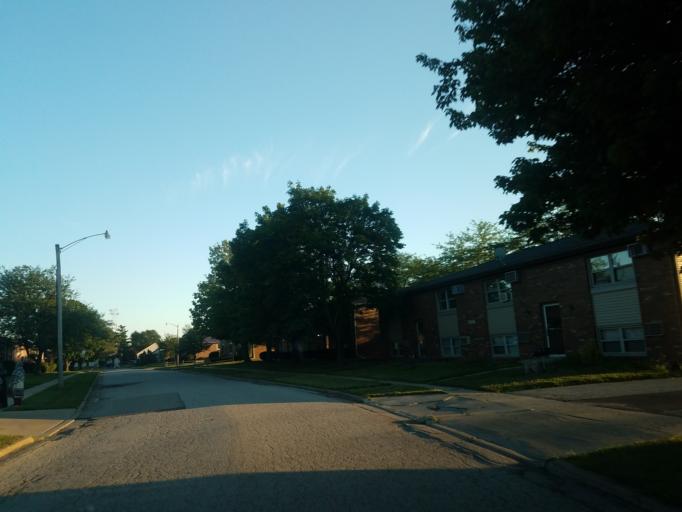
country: US
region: Illinois
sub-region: McLean County
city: Bloomington
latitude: 40.4713
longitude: -88.9508
